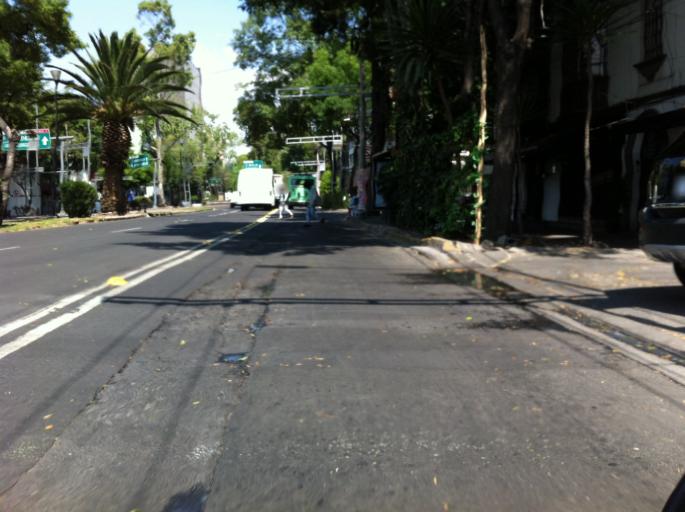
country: MX
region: Mexico City
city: Benito Juarez
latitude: 19.4163
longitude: -99.1695
